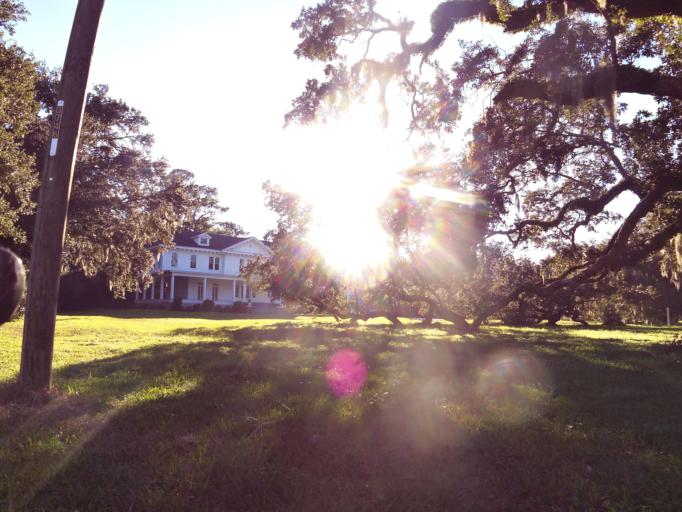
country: US
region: Florida
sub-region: Duval County
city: Jacksonville
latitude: 30.2809
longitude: -81.6992
